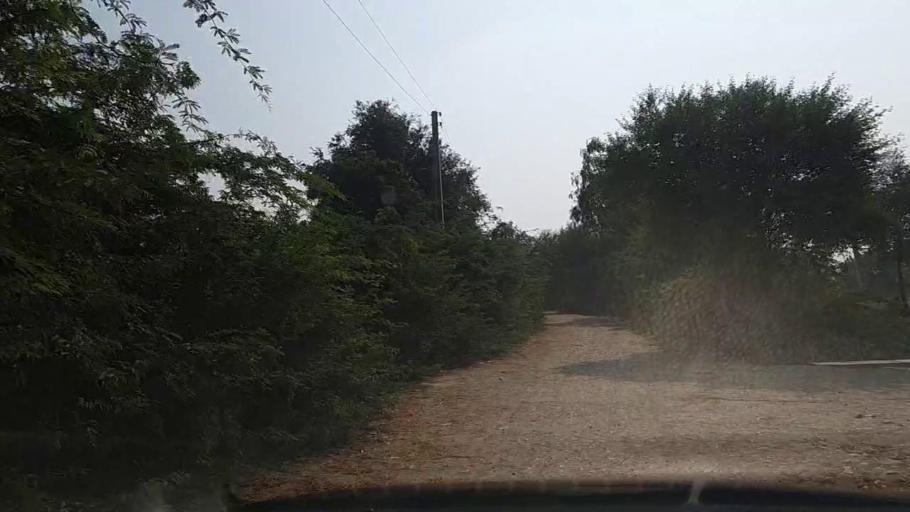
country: PK
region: Sindh
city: Mirpur Batoro
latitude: 24.6961
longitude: 68.2192
